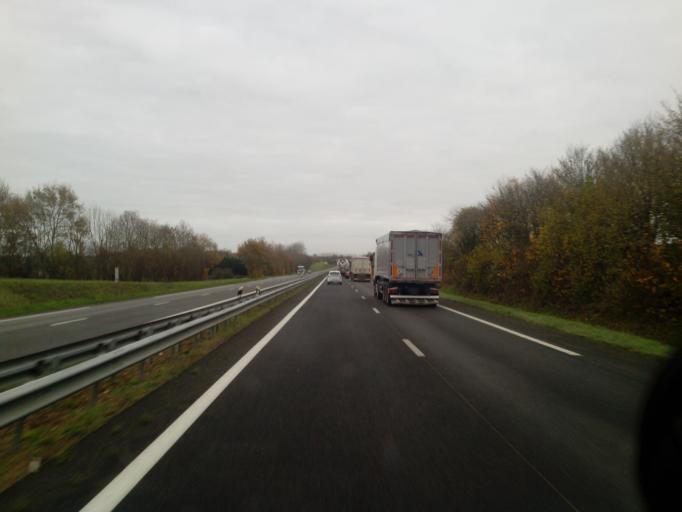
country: FR
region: Pays de la Loire
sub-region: Departement de Maine-et-Loire
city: Villedieu-la-Blouere
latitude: 47.1193
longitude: -1.0817
